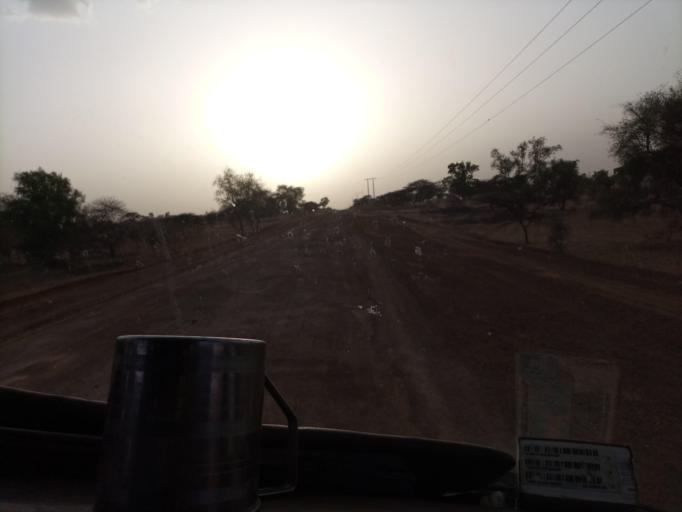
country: SN
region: Louga
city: Dara
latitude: 15.3954
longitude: -15.6440
